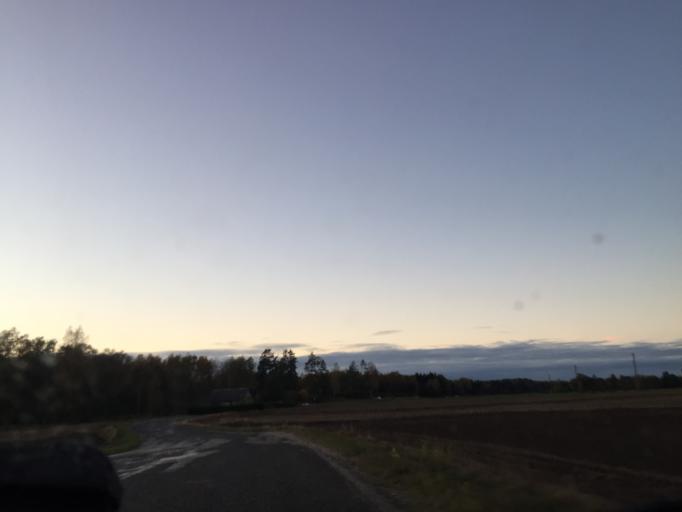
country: LV
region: Talsu Rajons
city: Sabile
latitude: 56.9659
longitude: 22.6067
